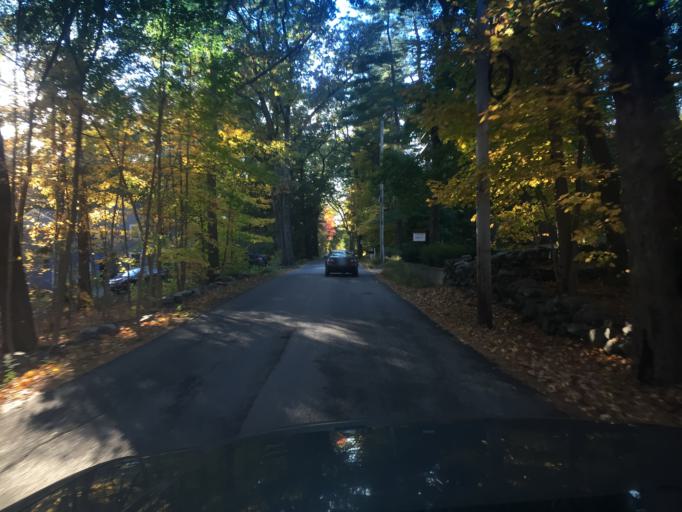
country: US
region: Massachusetts
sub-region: Middlesex County
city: Stow
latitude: 42.4079
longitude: -71.5187
